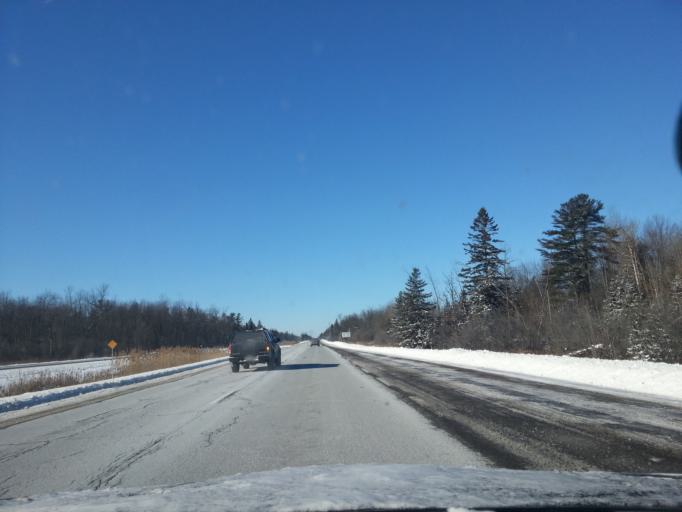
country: CA
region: Ontario
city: Carleton Place
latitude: 45.3152
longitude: -76.0675
